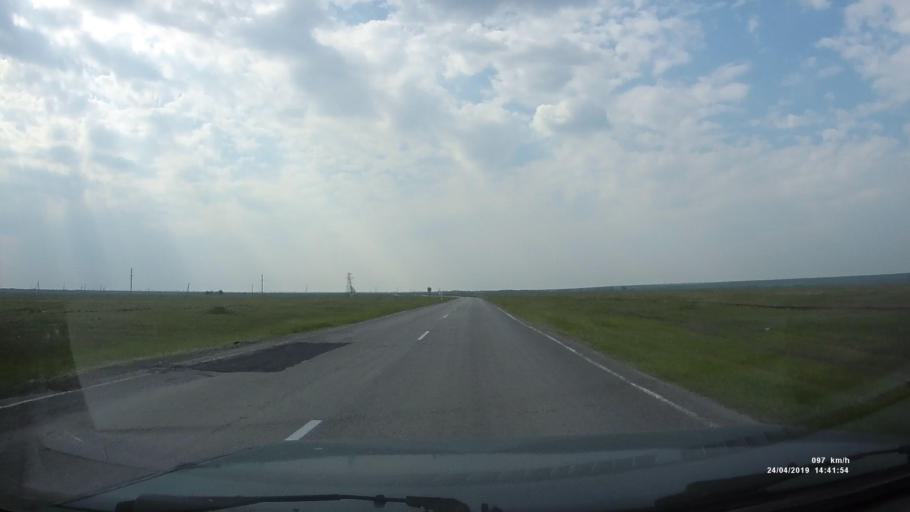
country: RU
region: Rostov
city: Remontnoye
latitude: 46.4490
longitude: 43.8722
